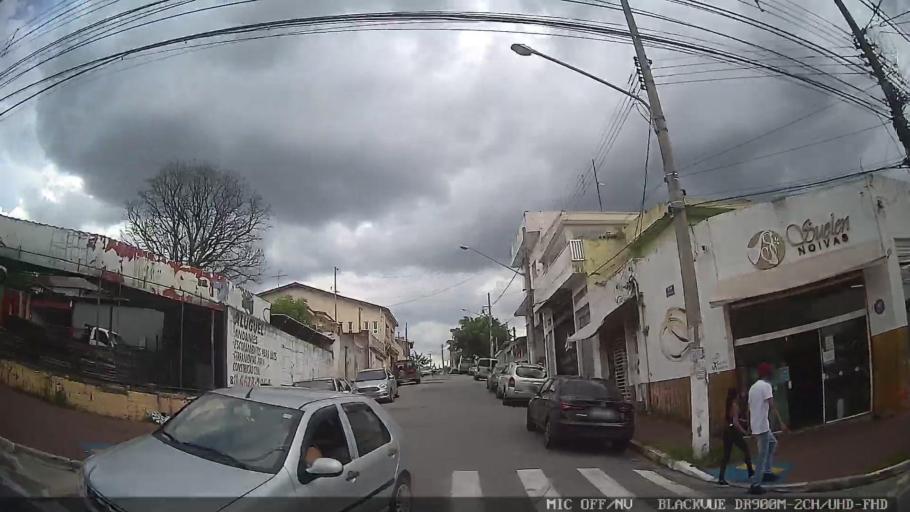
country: BR
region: Sao Paulo
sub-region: Ferraz De Vasconcelos
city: Ferraz de Vasconcelos
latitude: -23.5369
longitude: -46.3606
